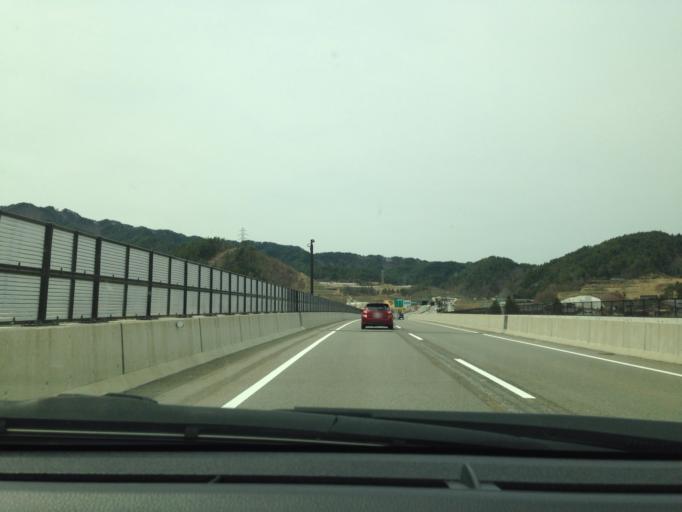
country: JP
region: Gifu
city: Takayama
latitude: 36.1638
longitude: 137.2352
